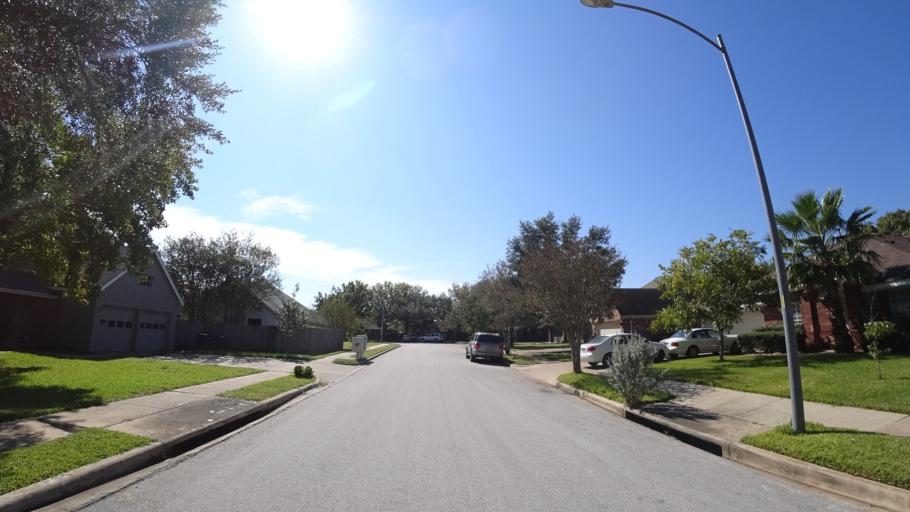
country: US
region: Texas
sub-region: Travis County
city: Shady Hollow
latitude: 30.2161
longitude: -97.8587
